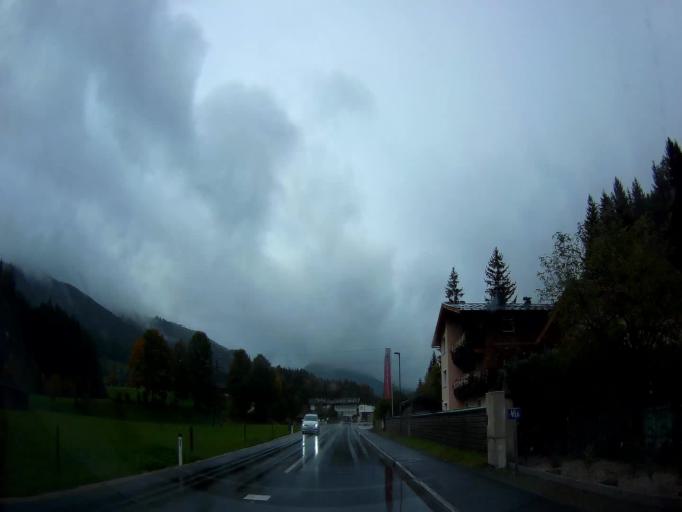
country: AT
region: Salzburg
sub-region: Politischer Bezirk Zell am See
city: Leogang
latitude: 47.4397
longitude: 12.7473
